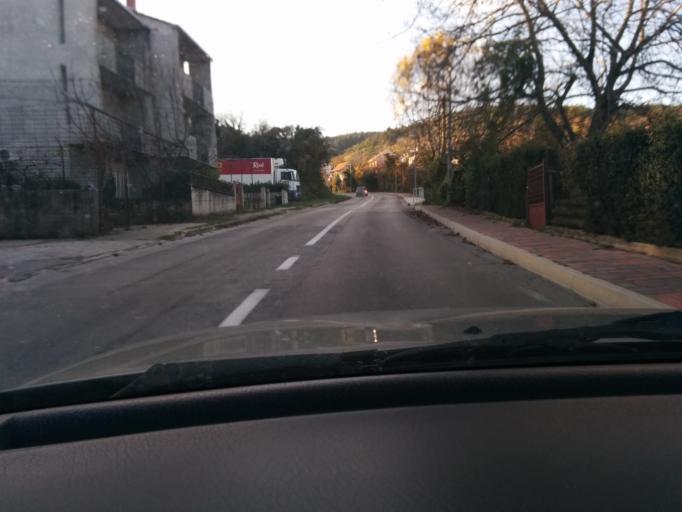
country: HR
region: Splitsko-Dalmatinska
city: Sinj
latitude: 43.7047
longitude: 16.6331
